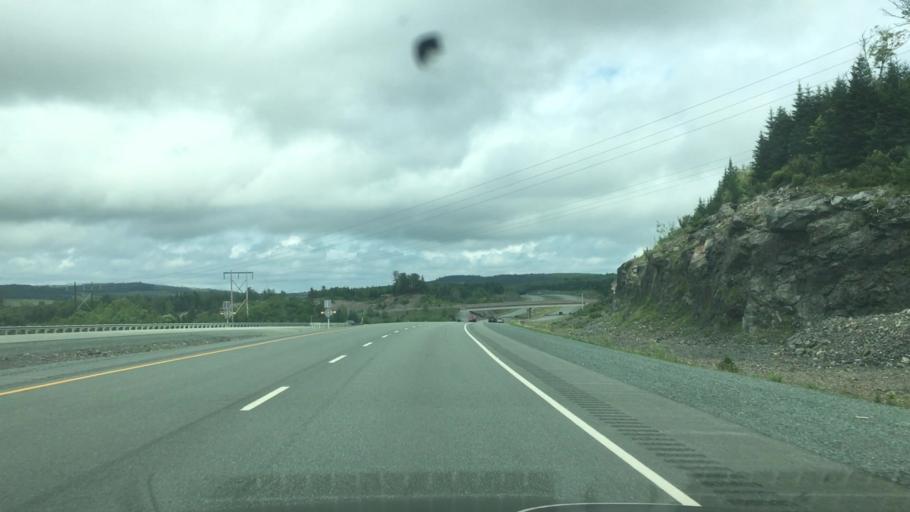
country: CA
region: Nova Scotia
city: Oxford
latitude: 45.5336
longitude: -63.7105
